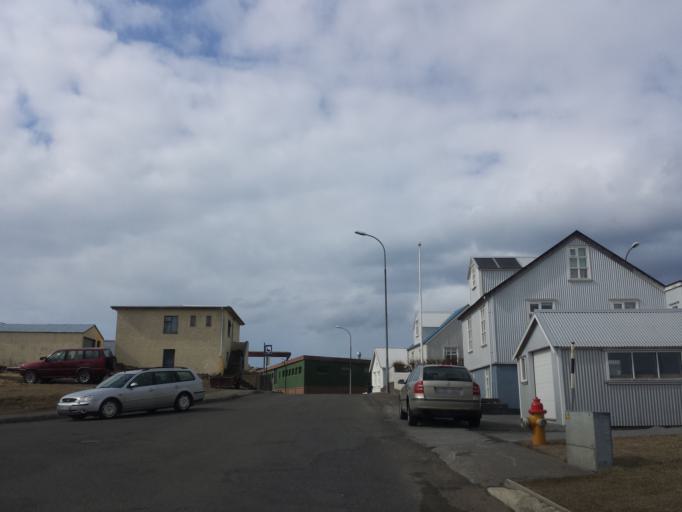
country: IS
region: West
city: Stykkisholmur
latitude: 65.0770
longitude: -22.7221
